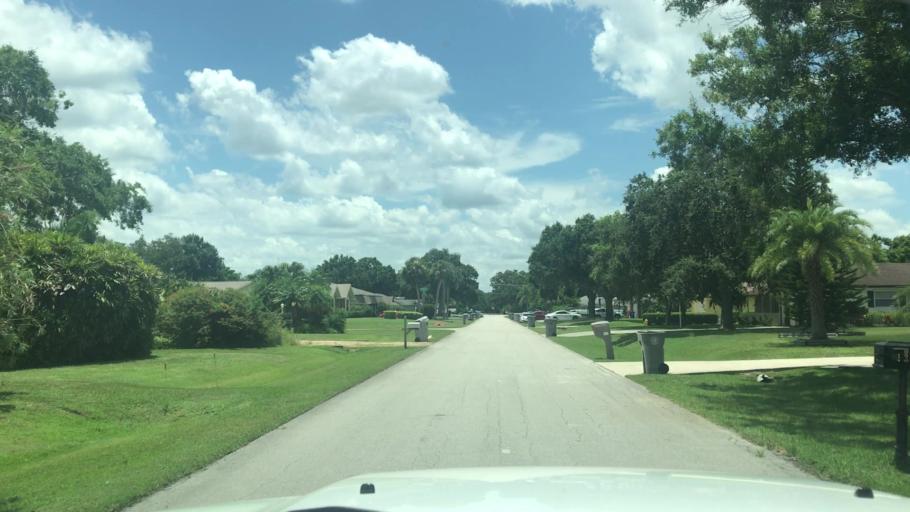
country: US
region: Florida
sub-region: Indian River County
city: Vero Beach South
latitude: 27.6262
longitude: -80.4158
